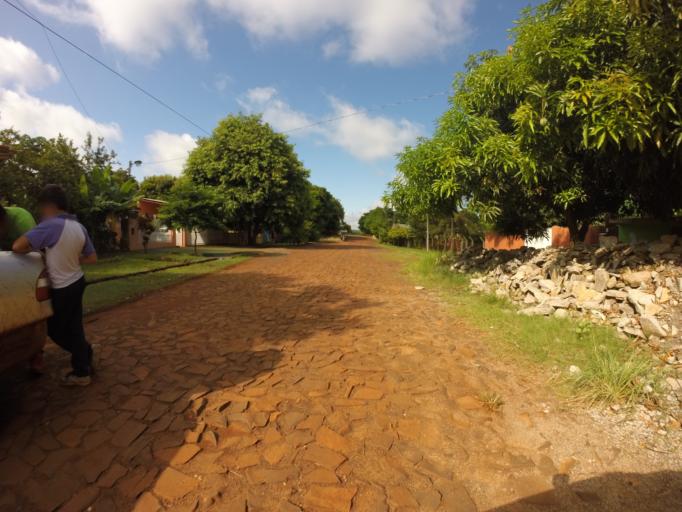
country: PY
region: Alto Parana
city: Ciudad del Este
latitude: -25.3997
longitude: -54.6467
